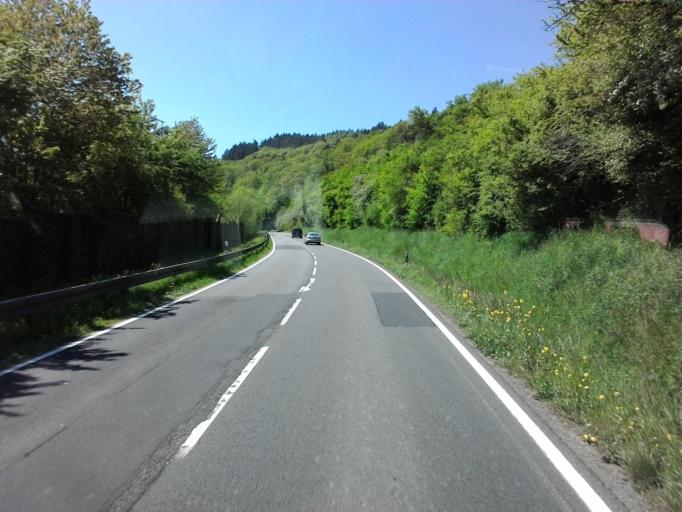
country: DE
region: Bavaria
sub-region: Regierungsbezirk Unterfranken
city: Lohr am Main
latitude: 49.9933
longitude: 9.5576
